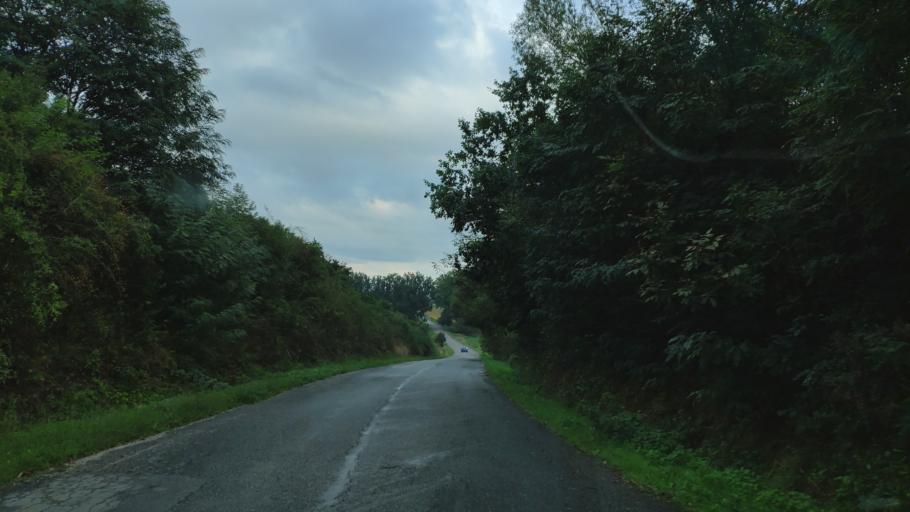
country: SK
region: Kosicky
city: Moldava nad Bodvou
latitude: 48.5826
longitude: 20.9299
